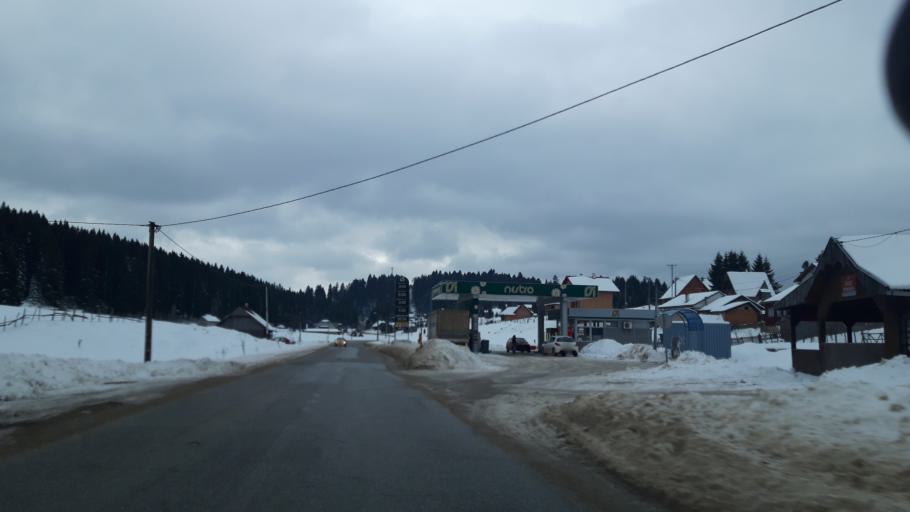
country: BA
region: Republika Srpska
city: Han Pijesak
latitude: 44.0952
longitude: 18.9570
